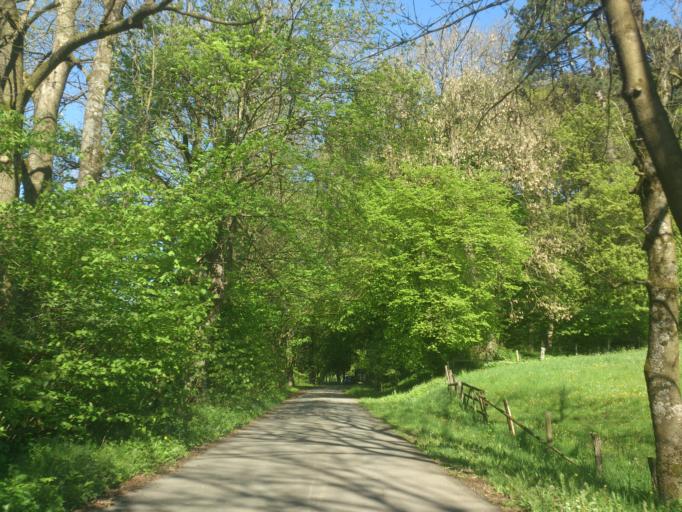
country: DE
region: North Rhine-Westphalia
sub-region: Regierungsbezirk Detmold
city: Bad Driburg
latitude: 51.6816
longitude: 8.9911
